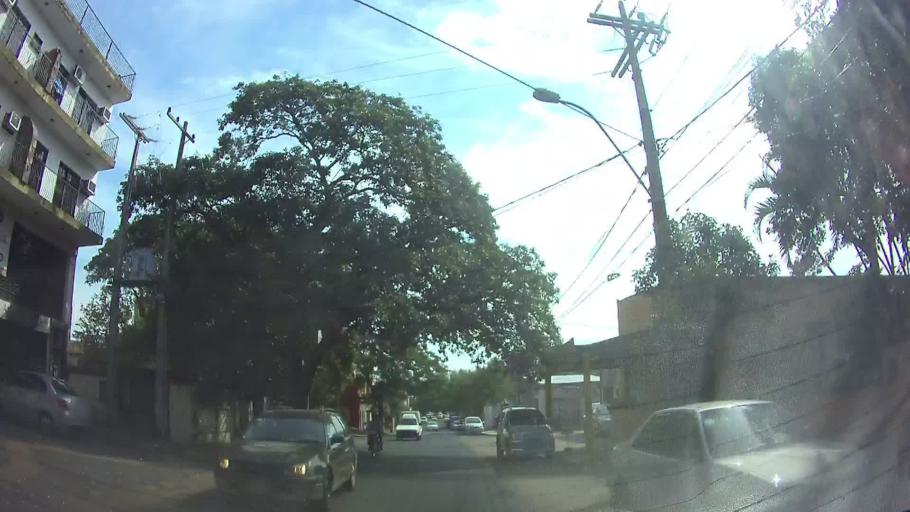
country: PY
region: Asuncion
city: Asuncion
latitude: -25.3027
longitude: -57.6117
